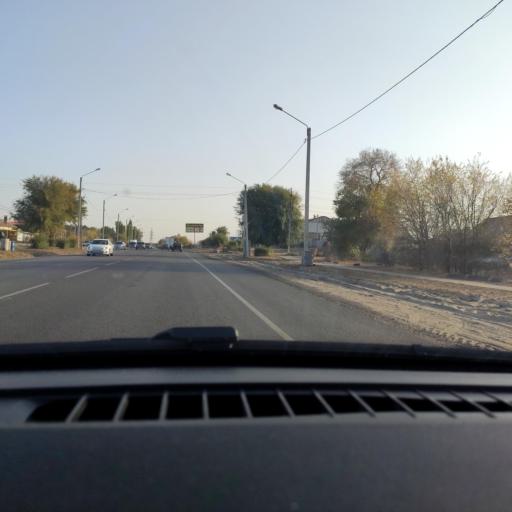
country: RU
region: Voronezj
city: Pridonskoy
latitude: 51.7048
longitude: 39.0757
